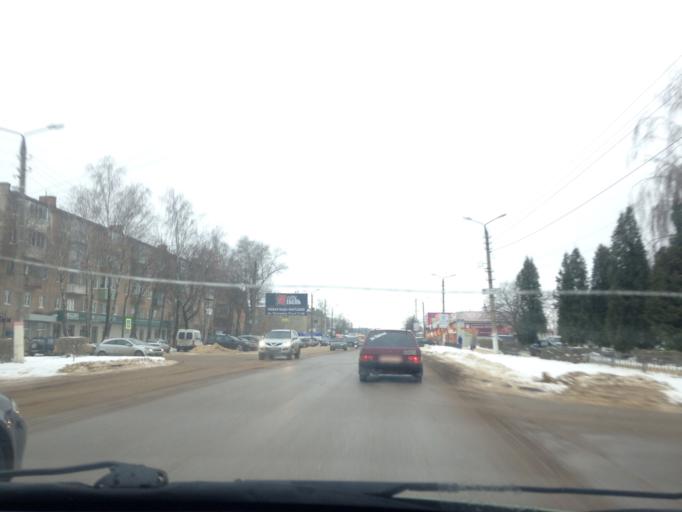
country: RU
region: Tula
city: Shchekino
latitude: 54.0130
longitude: 37.5152
